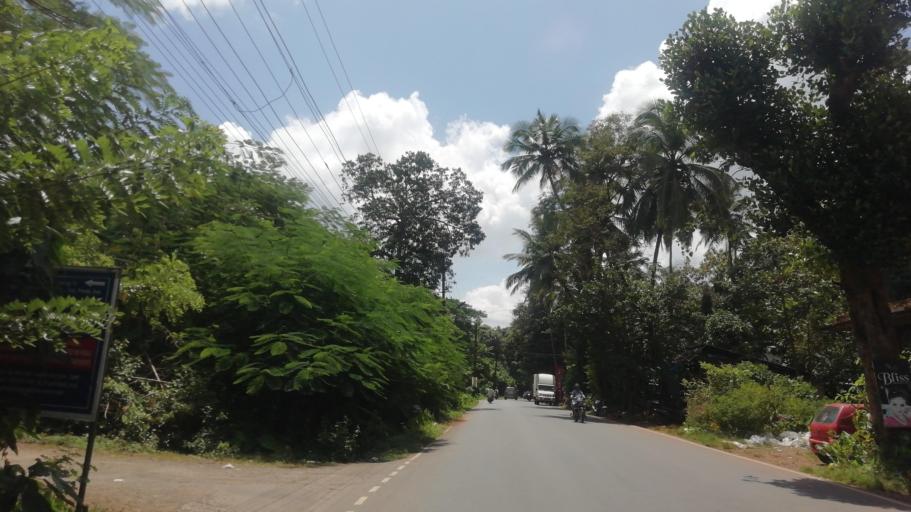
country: IN
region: Goa
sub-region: North Goa
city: Ponda
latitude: 15.3901
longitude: 74.0037
